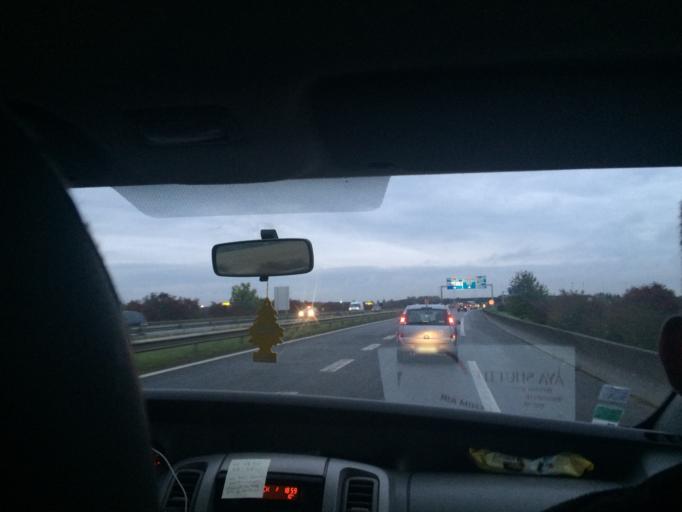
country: FR
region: Ile-de-France
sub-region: Departement du Val-d'Oise
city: Le Thillay
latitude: 48.9763
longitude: 2.4804
